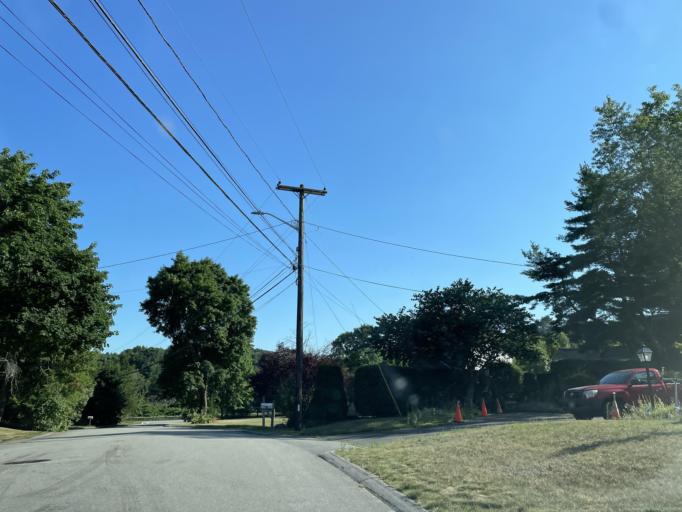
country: US
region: Massachusetts
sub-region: Norfolk County
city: Bellingham
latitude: 42.0929
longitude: -71.4363
